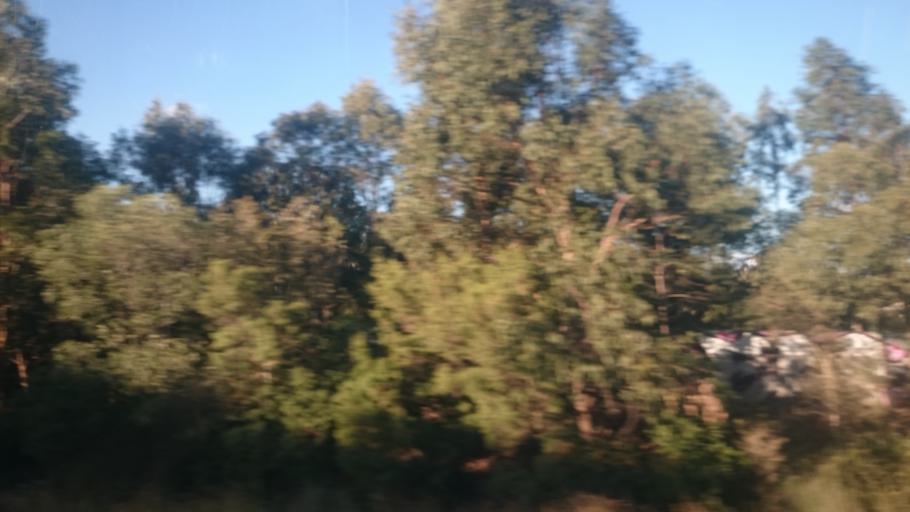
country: AU
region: Queensland
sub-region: Redland
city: Wellington Point
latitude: -27.5002
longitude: 153.2466
